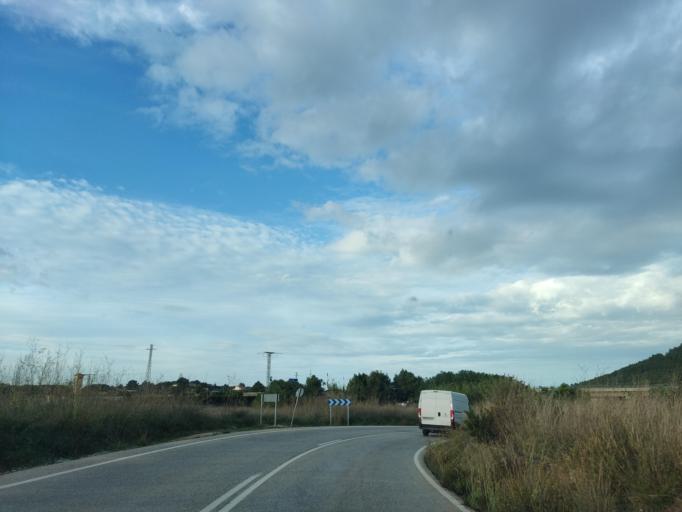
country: ES
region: Valencia
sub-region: Provincia de Alicante
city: Pedreguer
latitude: 38.8026
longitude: 0.0327
